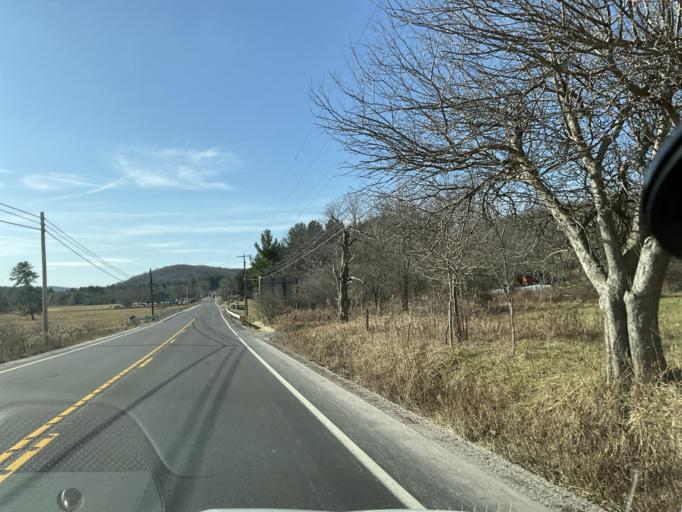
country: US
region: Maryland
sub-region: Garrett County
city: Oakland
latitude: 39.4004
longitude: -79.4276
